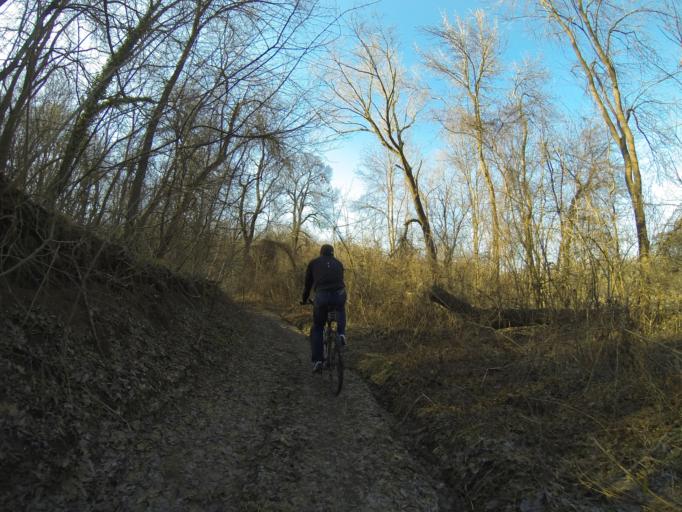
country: RO
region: Dolj
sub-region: Comuna Tuglui
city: Tuglui
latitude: 44.1620
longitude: 23.8269
